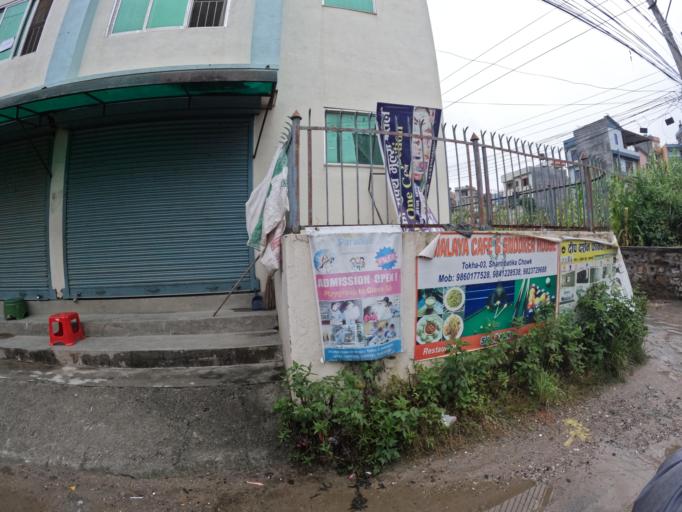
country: NP
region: Central Region
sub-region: Bagmati Zone
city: Kathmandu
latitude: 27.7571
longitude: 85.3199
